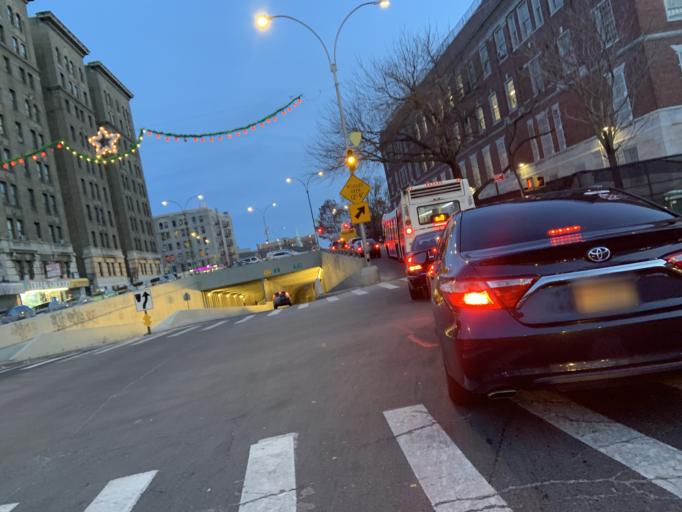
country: US
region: New York
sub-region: New York County
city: Inwood
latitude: 40.8667
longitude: -73.8956
